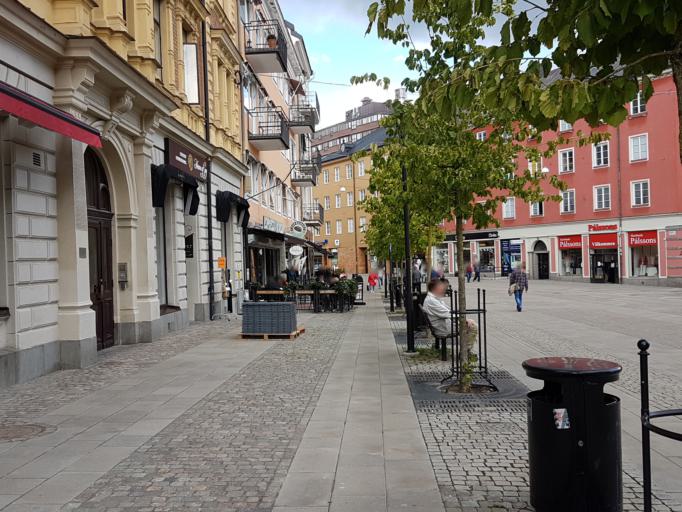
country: SE
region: Stockholm
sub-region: Sodertalje Kommun
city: Soedertaelje
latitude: 59.1947
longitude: 17.6279
